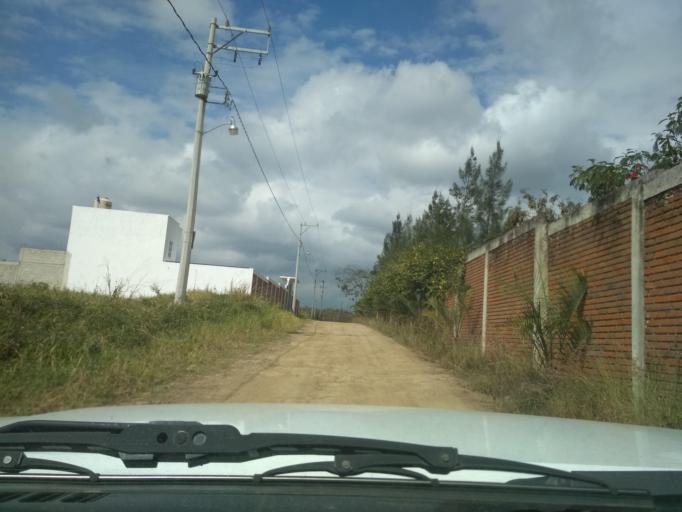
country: MX
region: Veracruz
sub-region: Emiliano Zapata
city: Jacarandas
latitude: 19.5022
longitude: -96.8251
